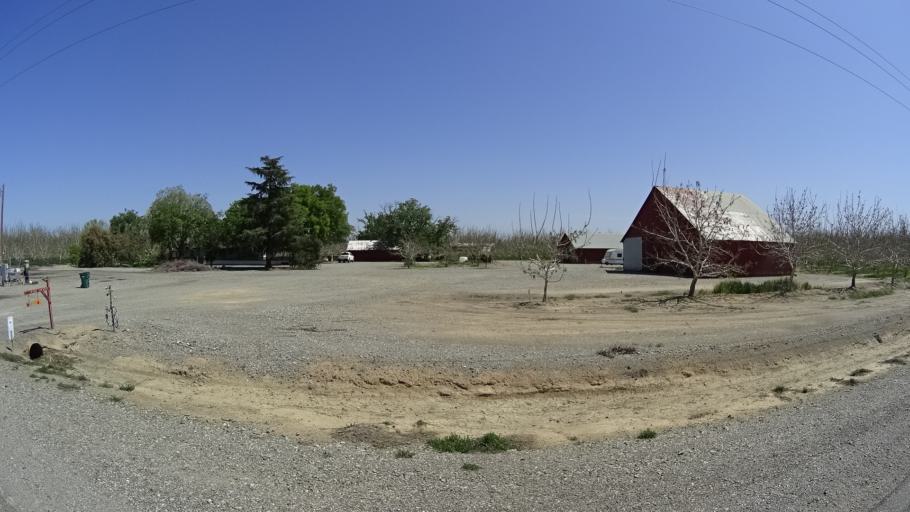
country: US
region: California
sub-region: Glenn County
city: Orland
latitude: 39.6590
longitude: -122.1971
